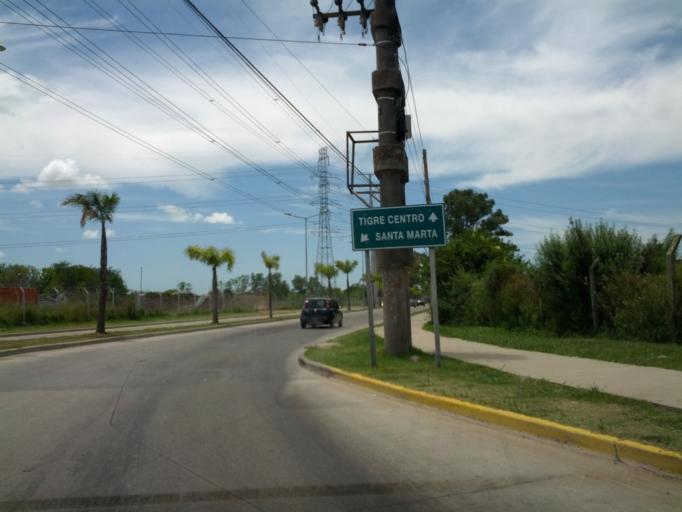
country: AR
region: Buenos Aires
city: Santa Catalina - Dique Lujan
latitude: -34.3974
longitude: -58.6695
